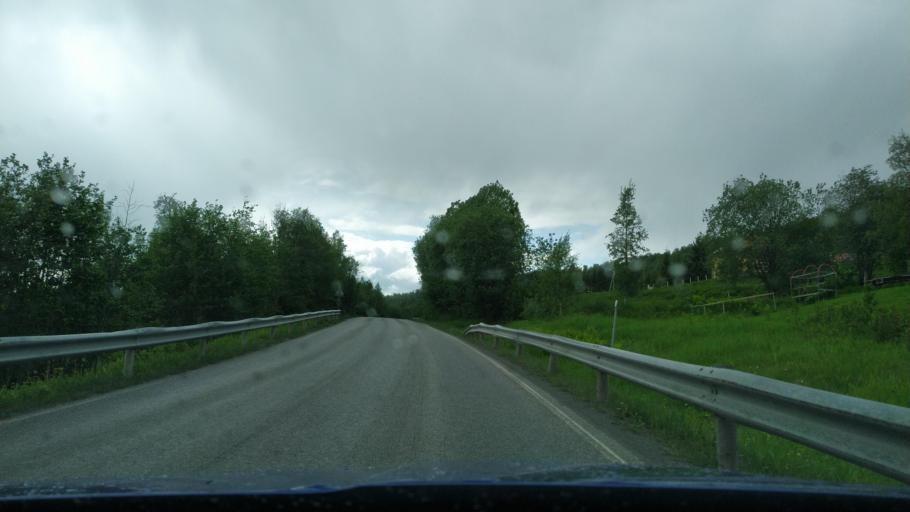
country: NO
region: Troms
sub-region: Sorreisa
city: Sorreisa
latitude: 69.1588
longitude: 18.1573
